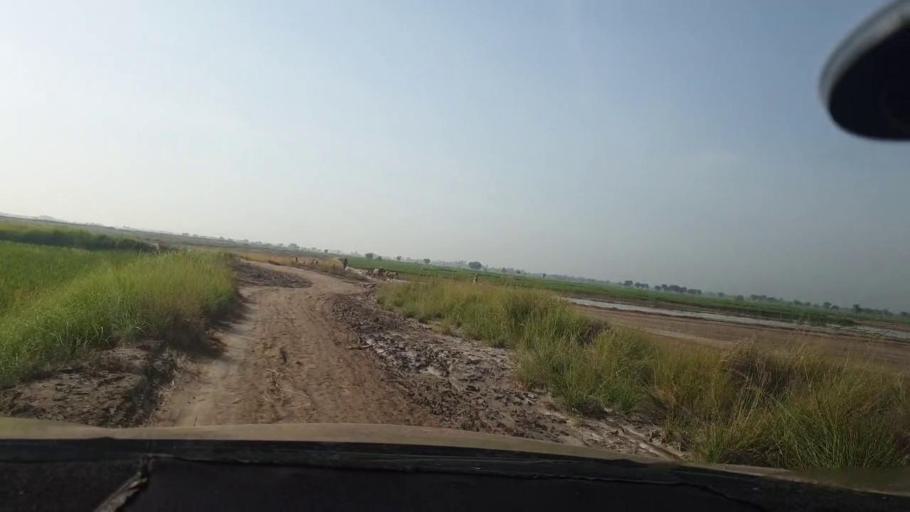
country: PK
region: Sindh
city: Kambar
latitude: 27.6422
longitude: 68.0494
